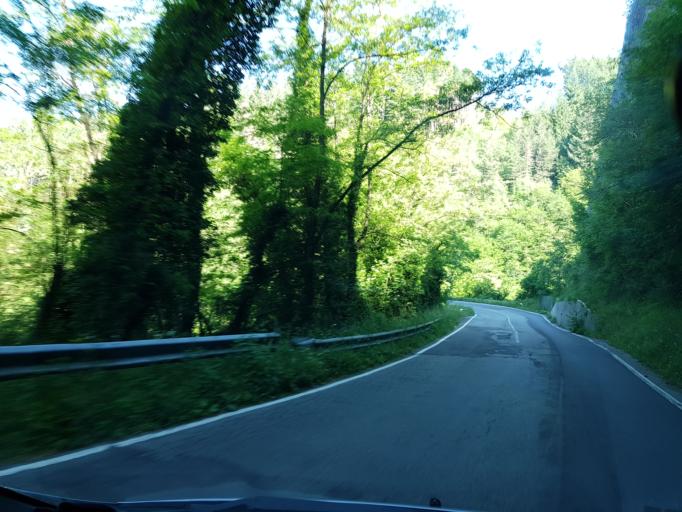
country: IT
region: Tuscany
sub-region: Provincia di Lucca
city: Camporgiano
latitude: 44.1727
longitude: 10.3262
